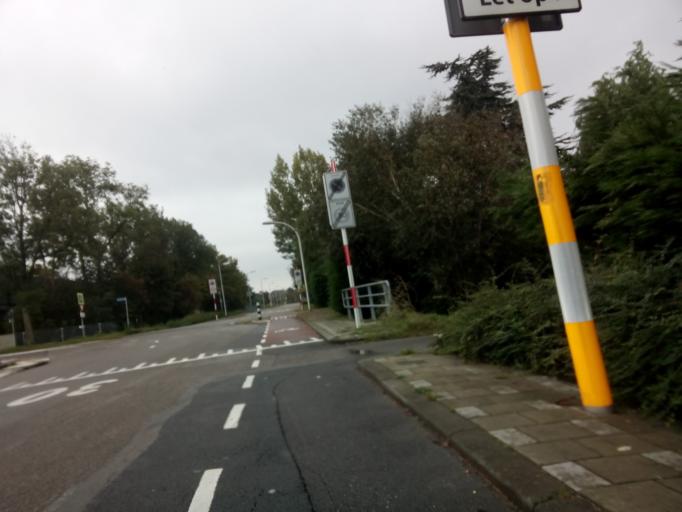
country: NL
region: South Holland
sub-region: Gemeente Den Haag
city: Ypenburg
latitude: 52.0455
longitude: 4.4046
